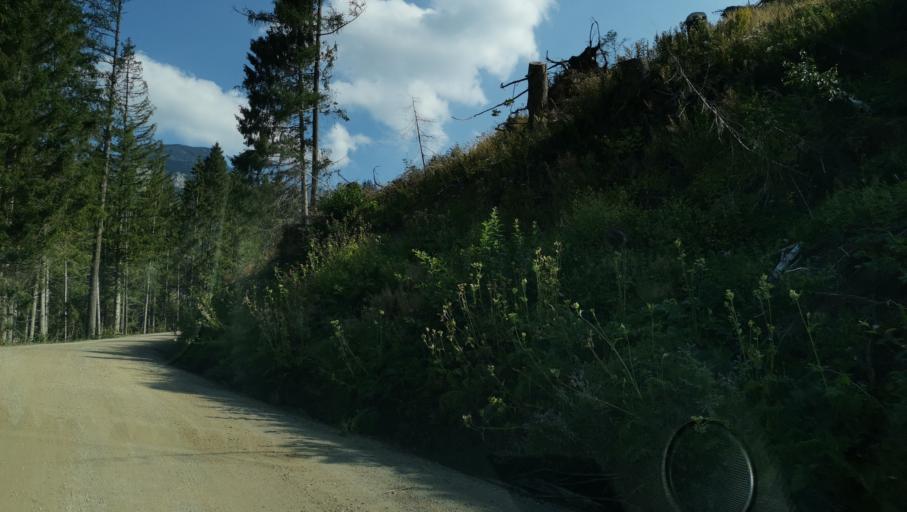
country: AT
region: Styria
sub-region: Politischer Bezirk Liezen
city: Trieben
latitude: 47.5290
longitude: 14.4881
